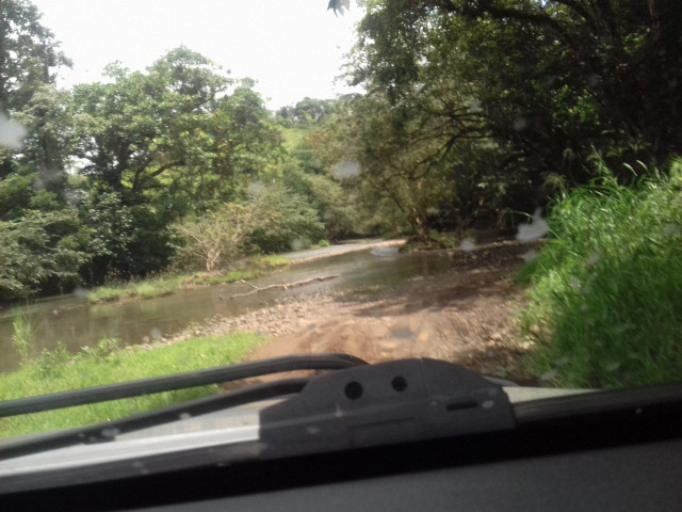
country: NI
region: Matagalpa
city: Rio Blanco
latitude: 12.9893
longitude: -85.3826
